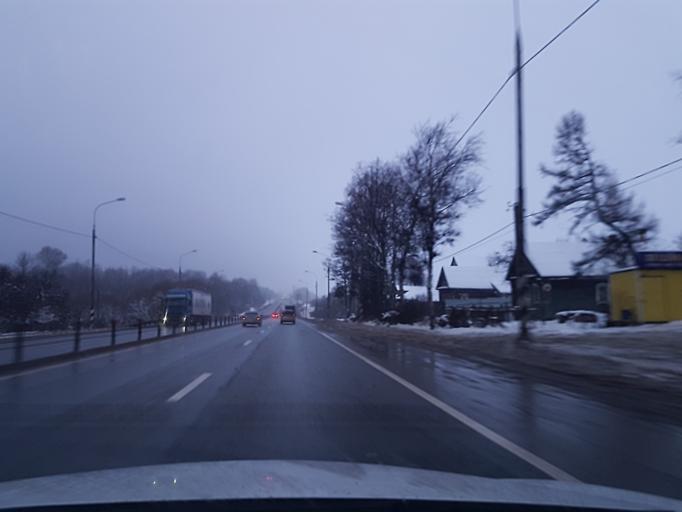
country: RU
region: Moskovskaya
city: Klin
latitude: 56.2885
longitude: 36.8145
